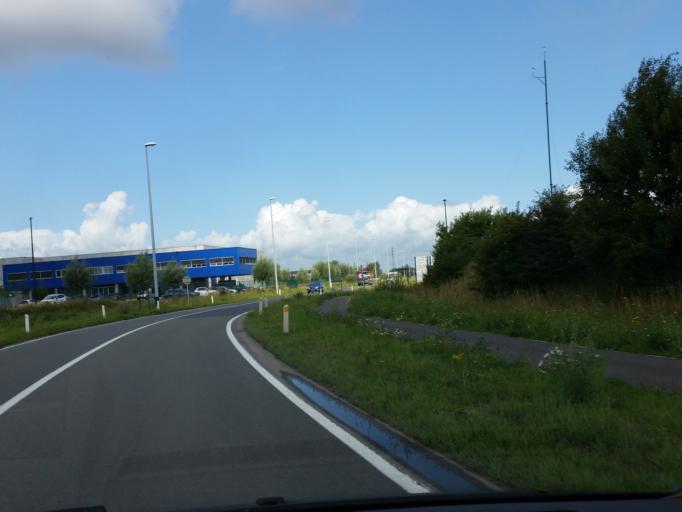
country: BE
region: Flanders
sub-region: Provincie West-Vlaanderen
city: Bredene
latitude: 51.2163
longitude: 2.9938
